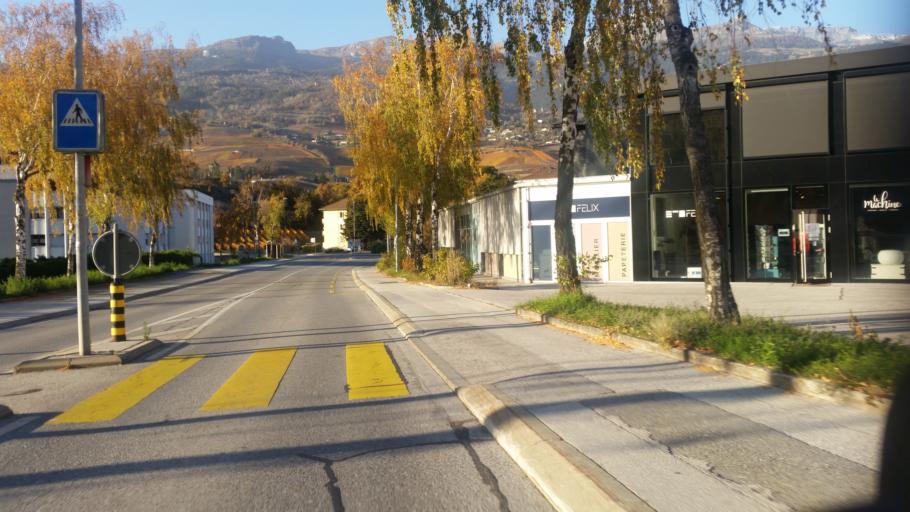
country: CH
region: Valais
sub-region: Sierre District
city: Sierre
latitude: 46.2881
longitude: 7.5359
